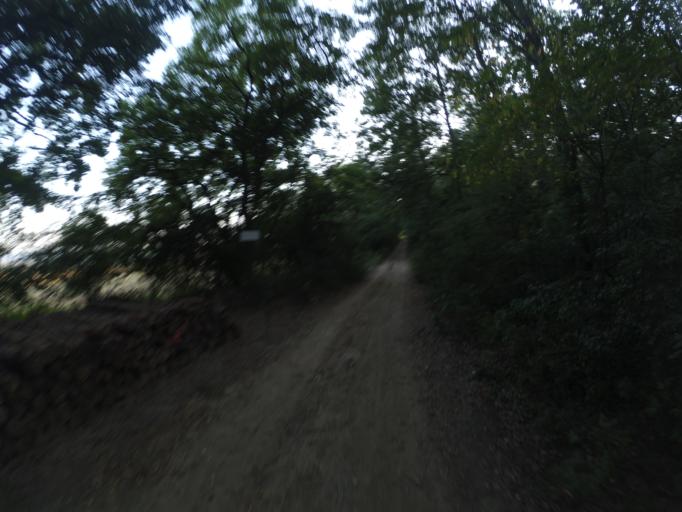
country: HU
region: Pest
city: Pilisszanto
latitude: 47.6709
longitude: 18.8753
